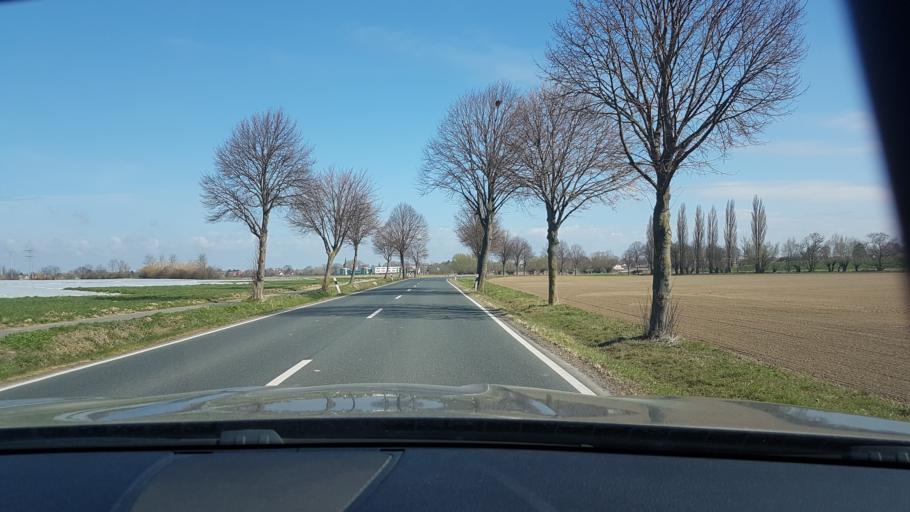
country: DE
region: Lower Saxony
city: Pattensen
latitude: 52.2512
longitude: 9.7463
